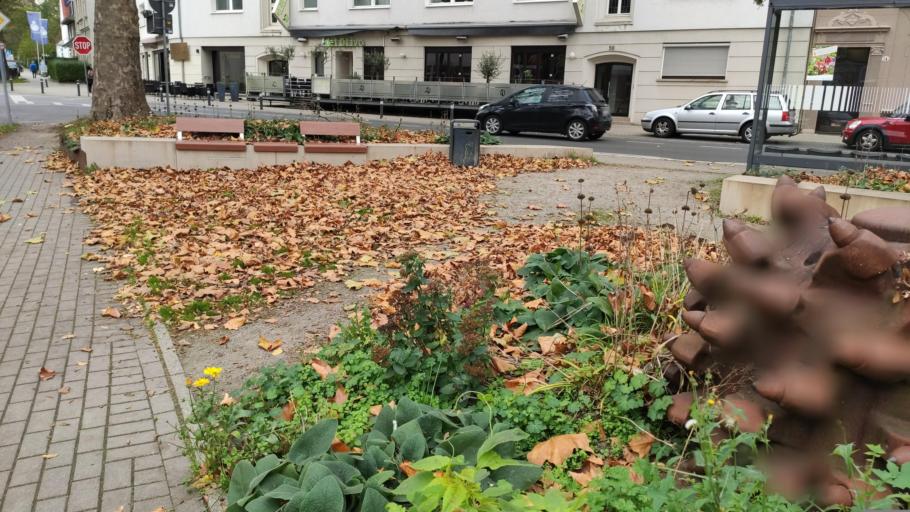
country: DE
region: North Rhine-Westphalia
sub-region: Regierungsbezirk Munster
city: Recklinghausen
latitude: 51.6159
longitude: 7.1877
